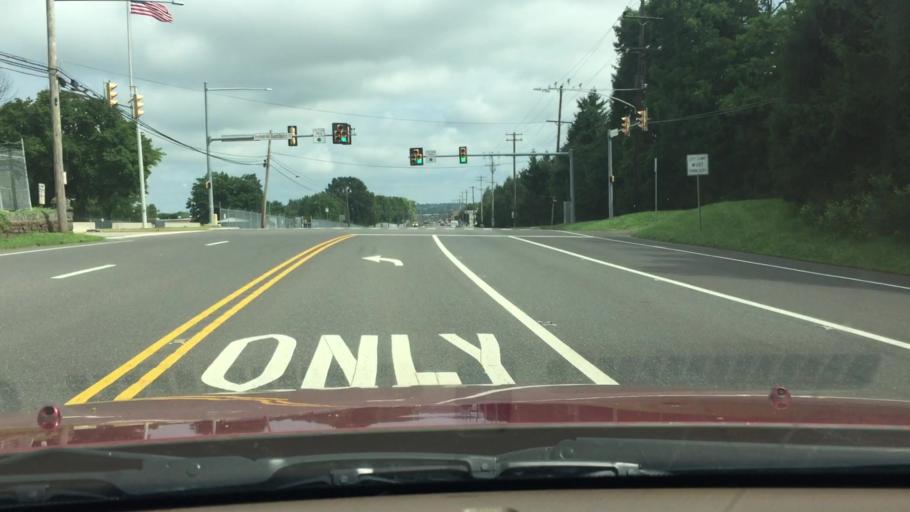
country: US
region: Pennsylvania
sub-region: Montgomery County
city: Horsham
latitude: 40.2054
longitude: -75.1398
